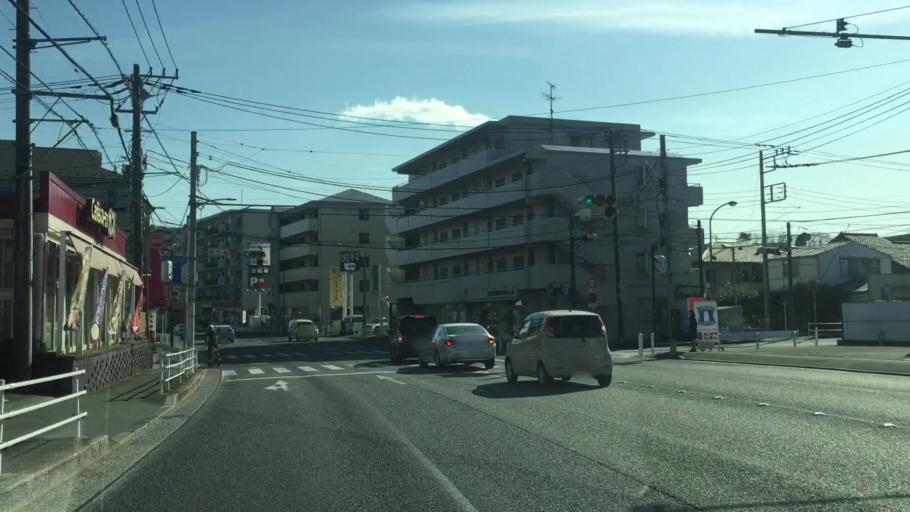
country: JP
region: Kanagawa
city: Zushi
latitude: 35.3474
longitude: 139.6084
